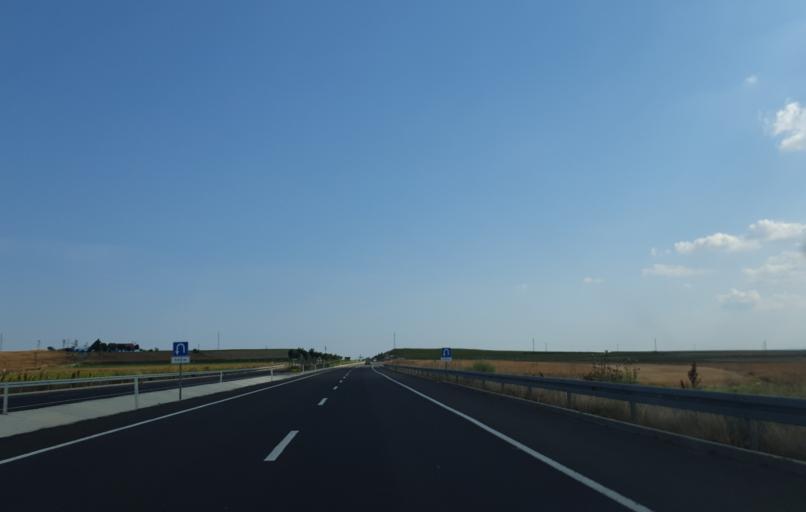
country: TR
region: Tekirdag
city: Muratli
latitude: 41.2144
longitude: 27.5335
